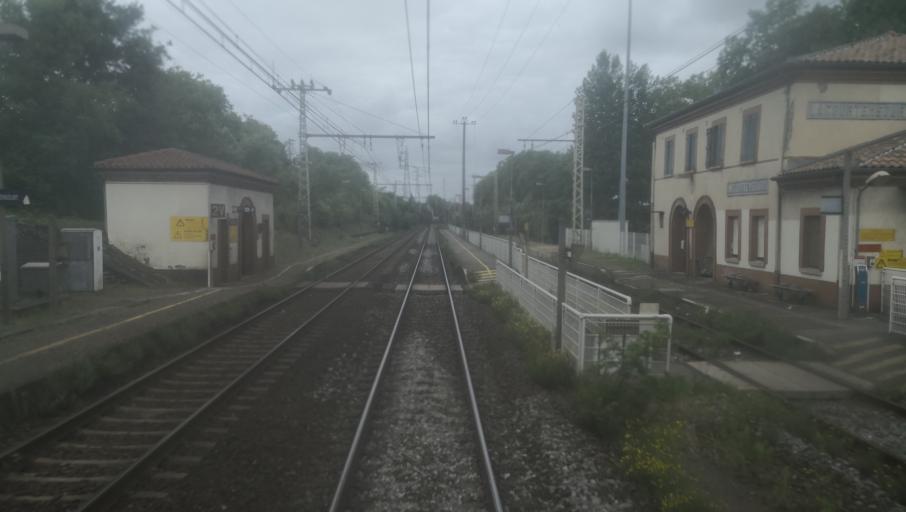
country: FR
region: Midi-Pyrenees
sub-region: Departement de la Haute-Garonne
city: Aucamville
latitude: 43.6637
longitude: 1.4141
